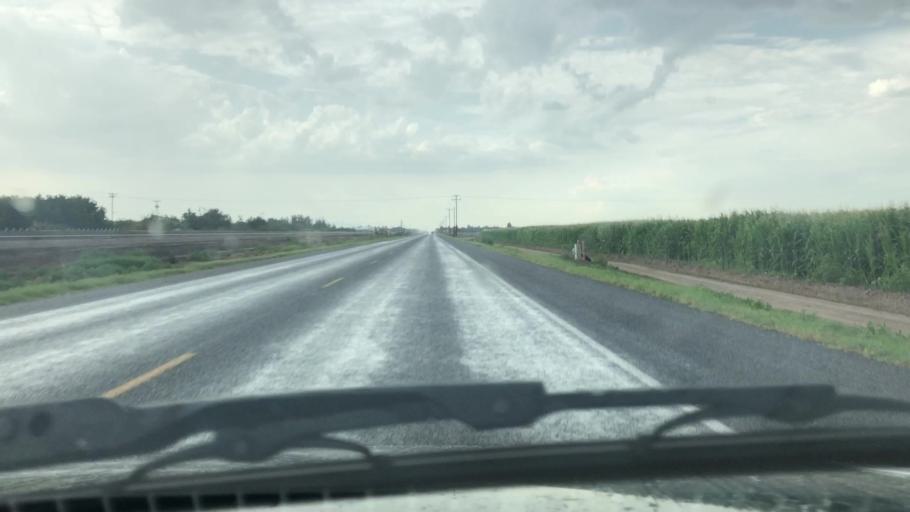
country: US
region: New Mexico
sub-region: Dona Ana County
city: Mesquite
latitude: 32.1511
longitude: -106.6881
